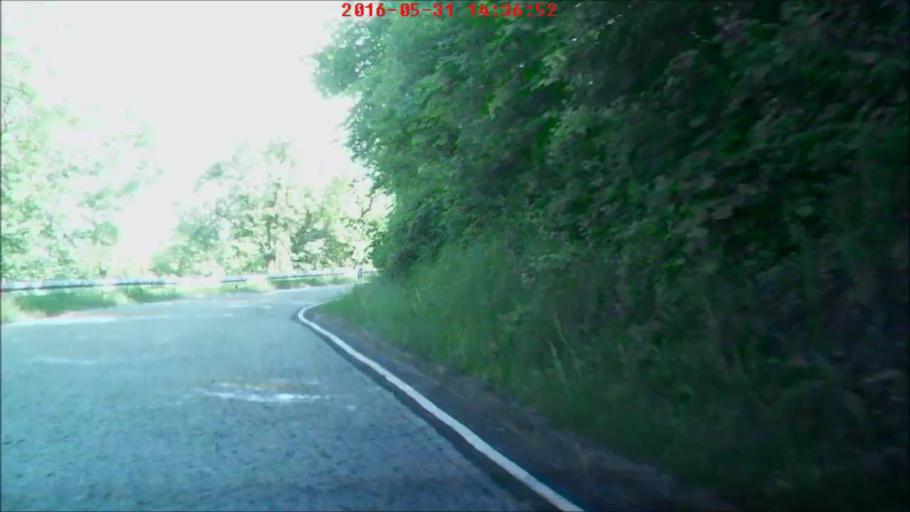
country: DE
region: Thuringia
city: Bilzingsleben
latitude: 51.3032
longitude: 11.0528
